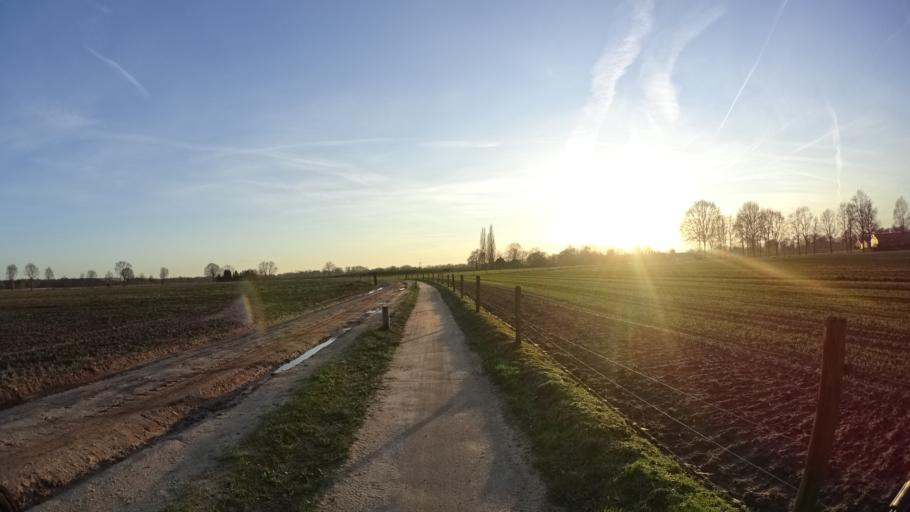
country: NL
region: Gelderland
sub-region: Gemeente Ede
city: Lunteren
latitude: 52.0726
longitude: 5.6439
